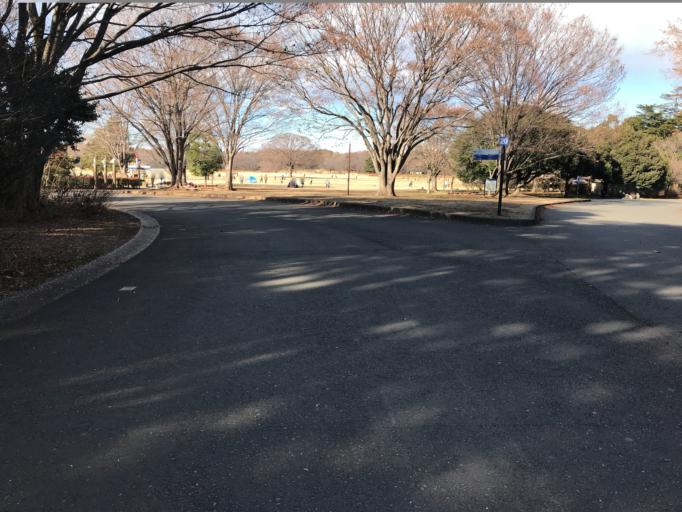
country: JP
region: Tokyo
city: Hino
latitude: 35.7085
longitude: 139.3975
